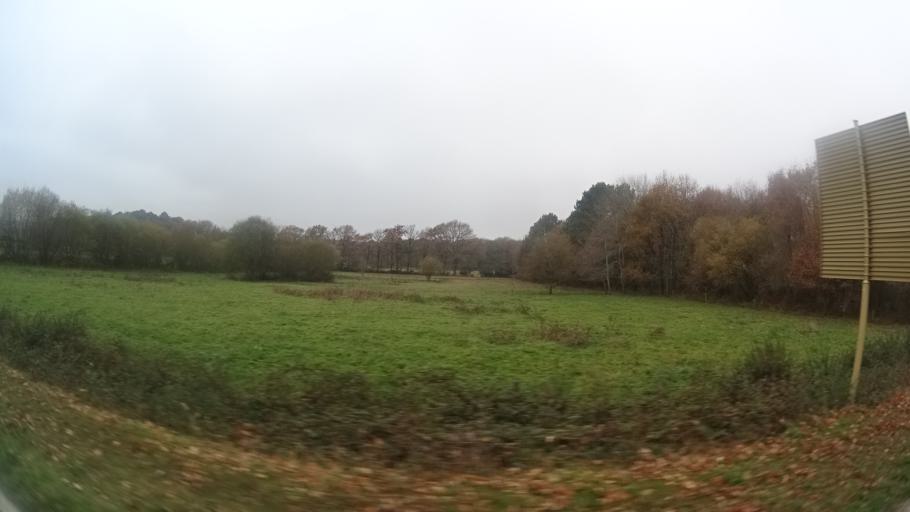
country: FR
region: Brittany
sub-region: Departement d'Ille-et-Vilaine
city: Bains-sur-Oust
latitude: 47.6921
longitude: -2.0574
